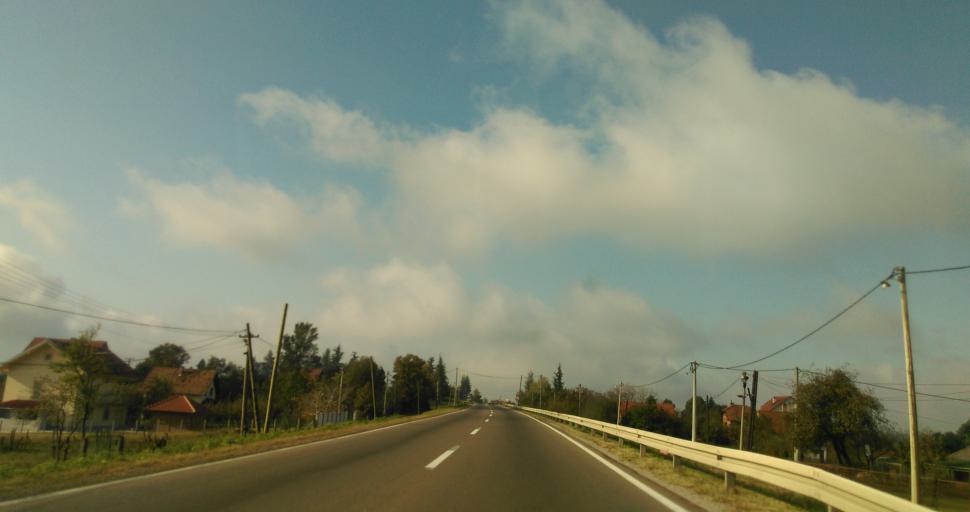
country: RS
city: Vranic
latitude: 44.5857
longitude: 20.3382
